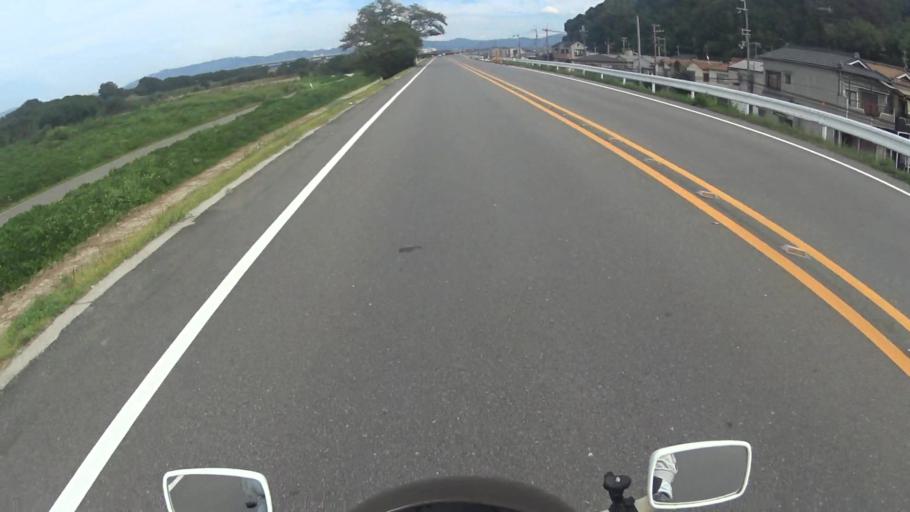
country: JP
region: Kyoto
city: Yawata
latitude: 34.8866
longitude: 135.6912
